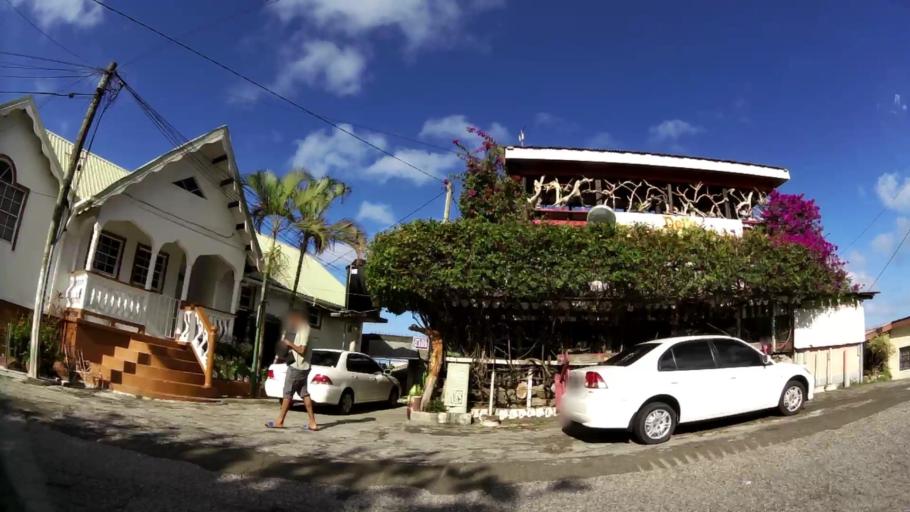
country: LC
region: Anse-la-Raye
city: Canaries
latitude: 13.9070
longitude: -61.0664
